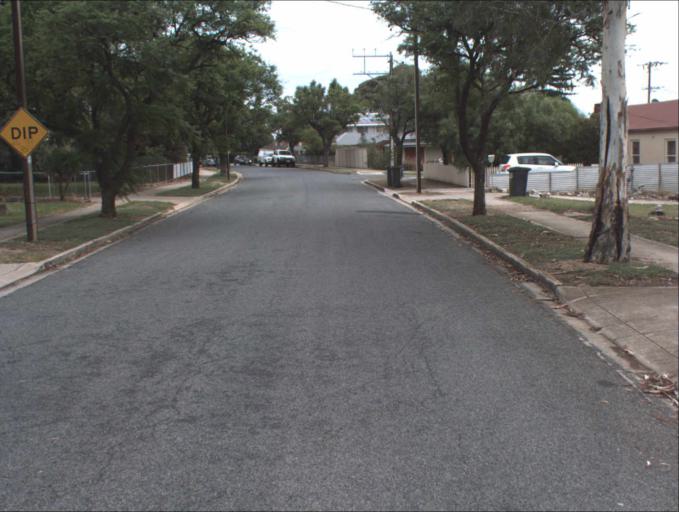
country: AU
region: South Australia
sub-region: Port Adelaide Enfield
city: Enfield
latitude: -34.8579
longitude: 138.6045
